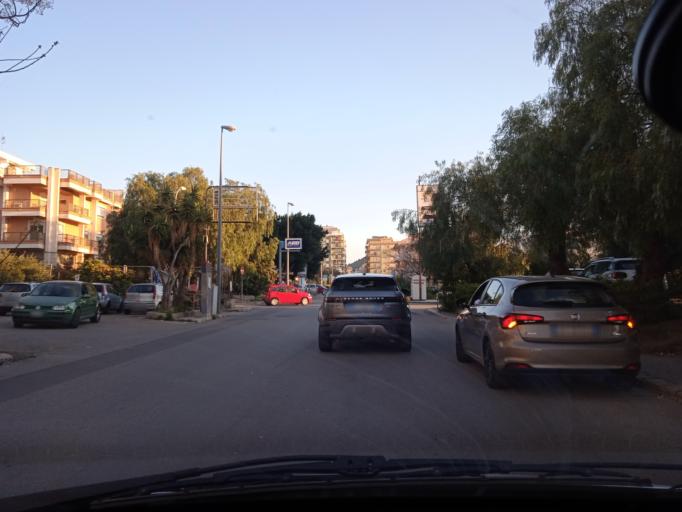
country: IT
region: Sicily
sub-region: Palermo
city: Bagheria
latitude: 38.0824
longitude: 13.5016
